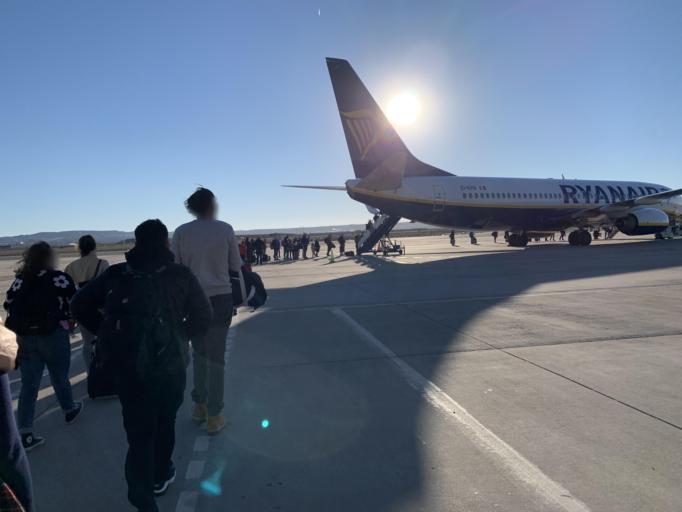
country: ES
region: Aragon
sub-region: Provincia de Zaragoza
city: Utebo
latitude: 41.6629
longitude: -1.0081
